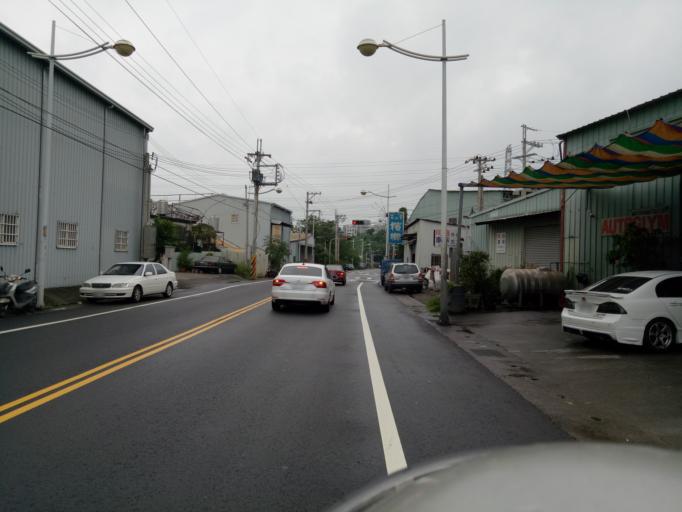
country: TW
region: Taiwan
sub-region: Taichung City
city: Taichung
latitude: 24.1104
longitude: 120.7129
